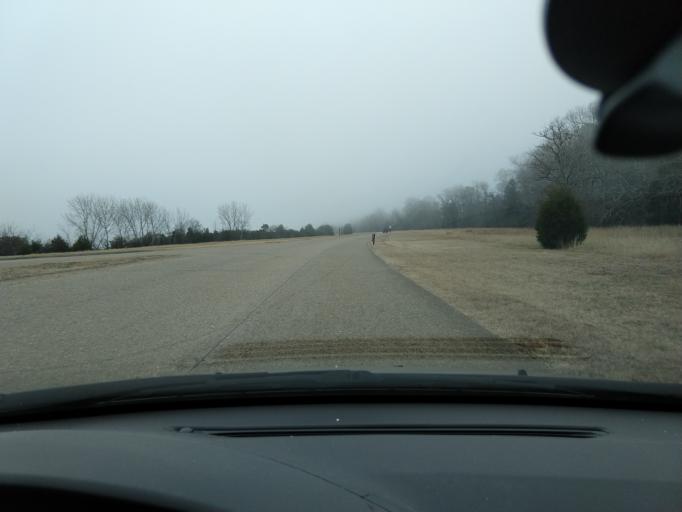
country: US
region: Virginia
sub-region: York County
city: Yorktown
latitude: 37.2673
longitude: -76.5544
